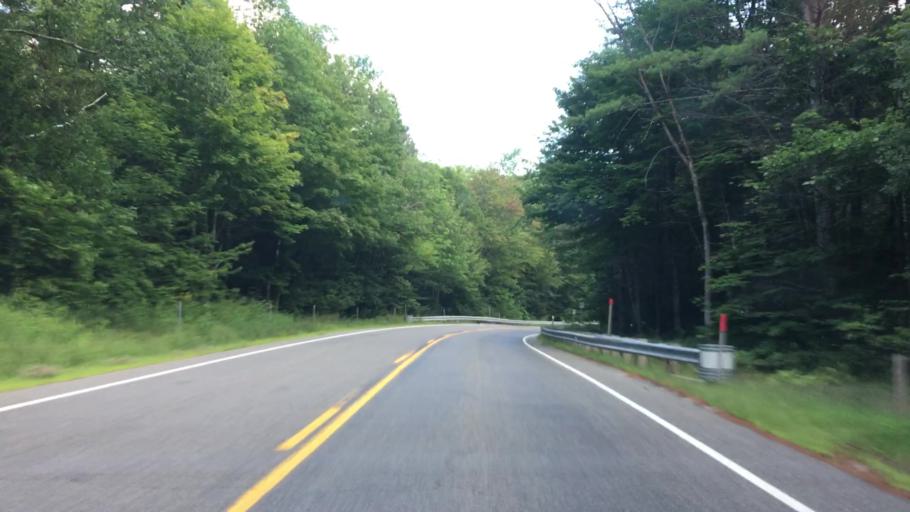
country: US
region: New Hampshire
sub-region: Grafton County
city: Woodstock
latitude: 44.0773
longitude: -71.7970
